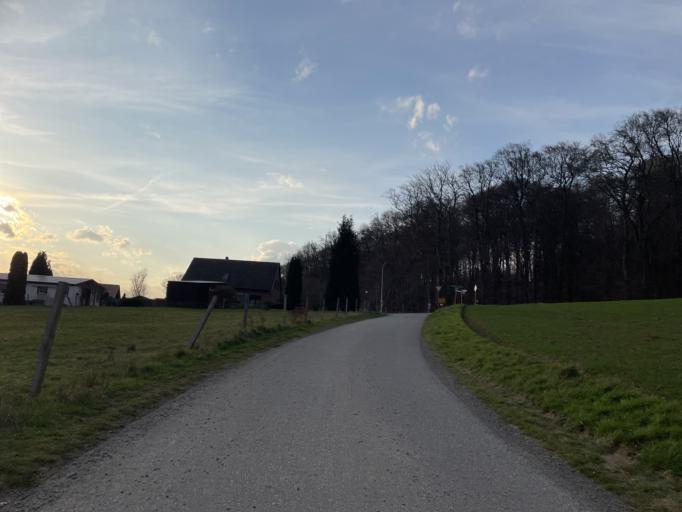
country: DE
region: North Rhine-Westphalia
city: Porta Westfalica
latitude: 52.2369
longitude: 8.9513
